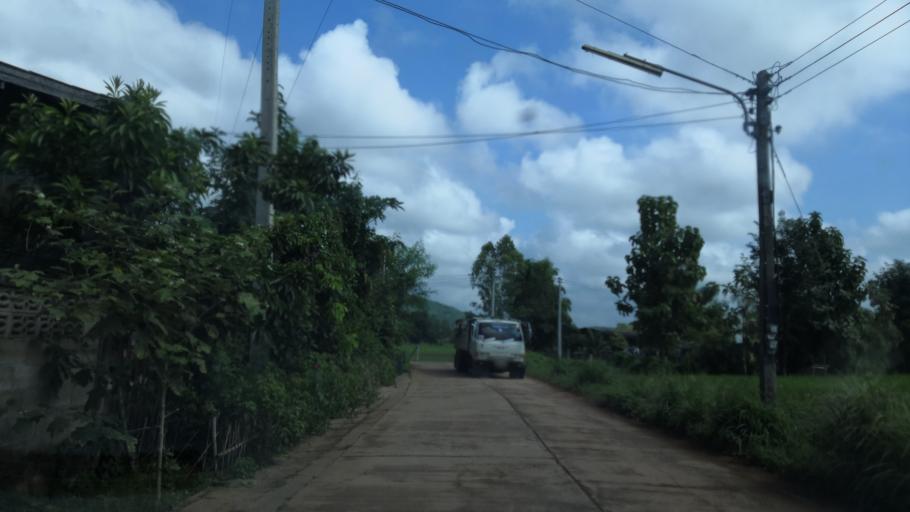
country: TH
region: Chiang Rai
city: Wiang Chiang Rung
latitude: 20.0144
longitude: 100.0406
